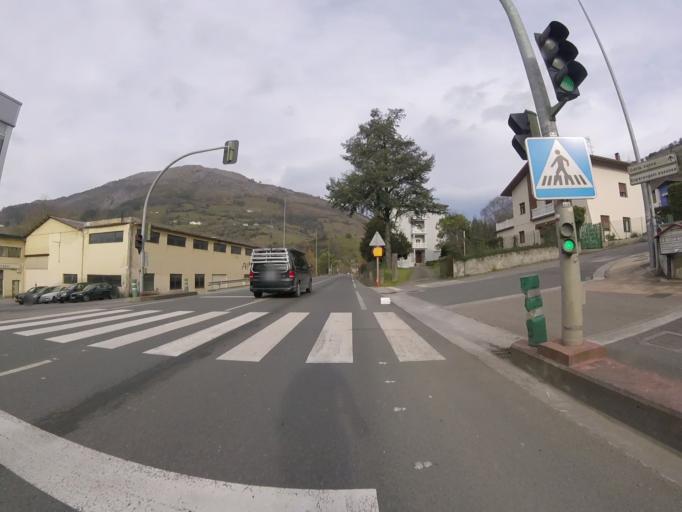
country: ES
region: Basque Country
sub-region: Provincia de Guipuzcoa
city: Azpeitia
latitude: 43.1845
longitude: -2.2602
